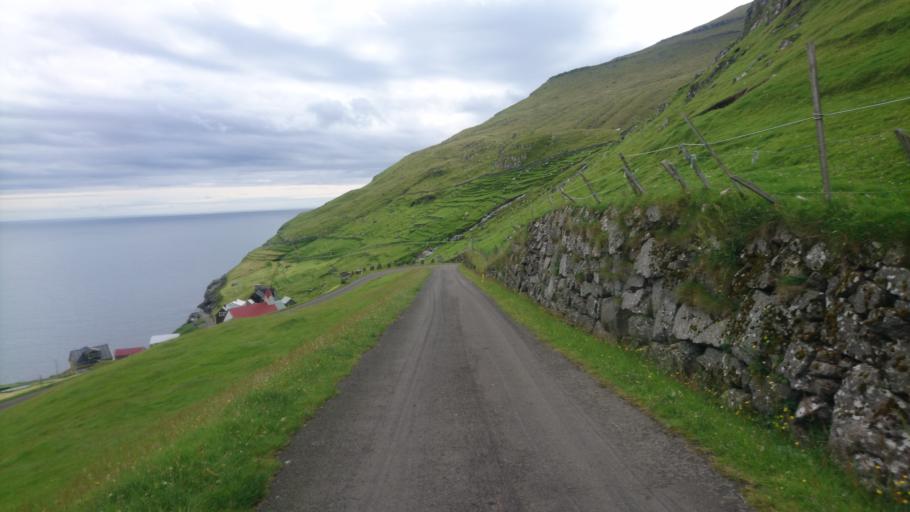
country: FO
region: Nordoyar
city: Klaksvik
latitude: 62.3308
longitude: -6.2778
